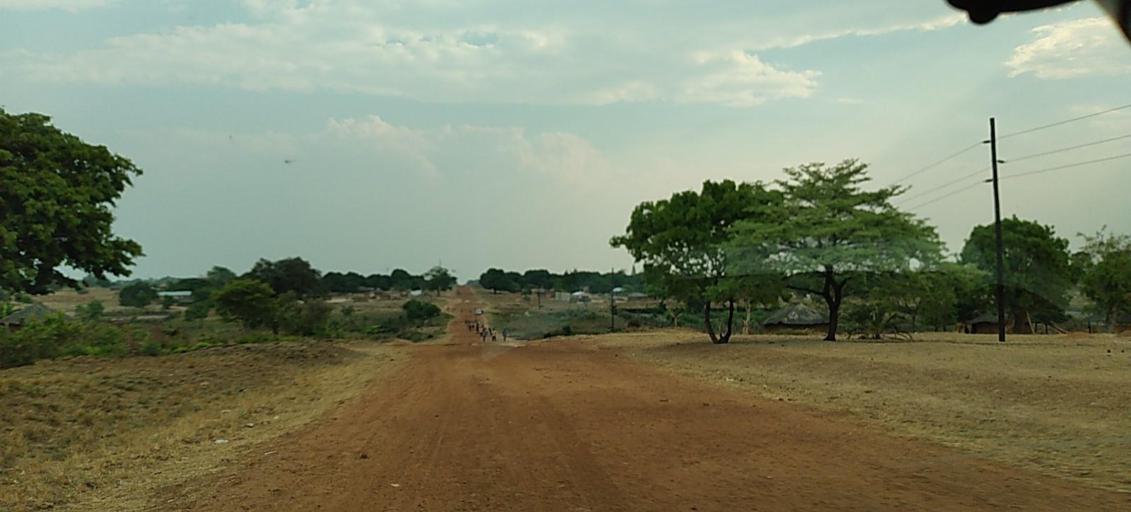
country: ZM
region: North-Western
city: Kabompo
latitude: -13.8646
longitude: 23.6706
